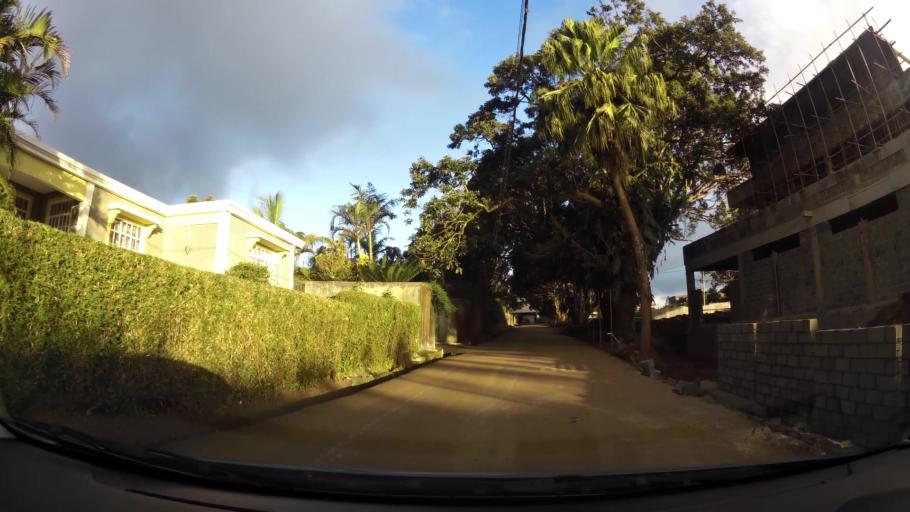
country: MU
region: Plaines Wilhems
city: Curepipe
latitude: -20.3136
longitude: 57.5286
